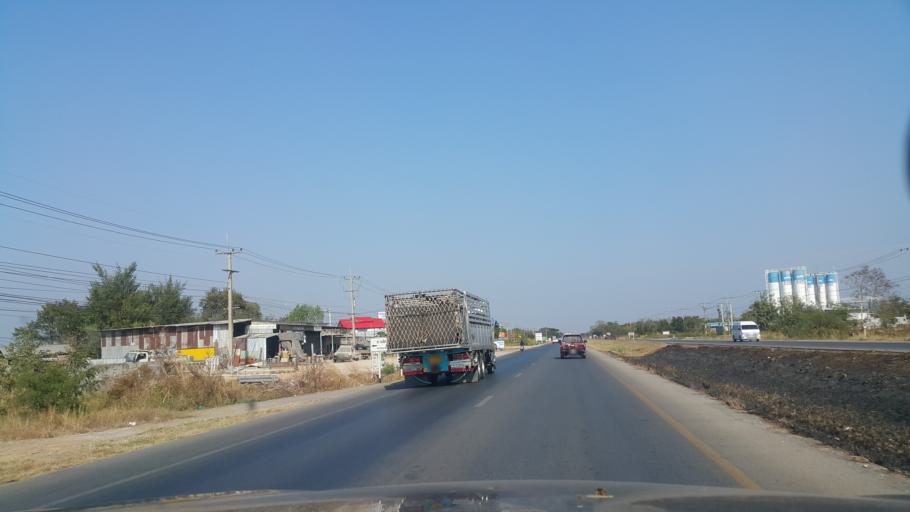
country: TH
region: Khon Kaen
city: Khon Kaen
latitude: 16.4020
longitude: 102.8744
